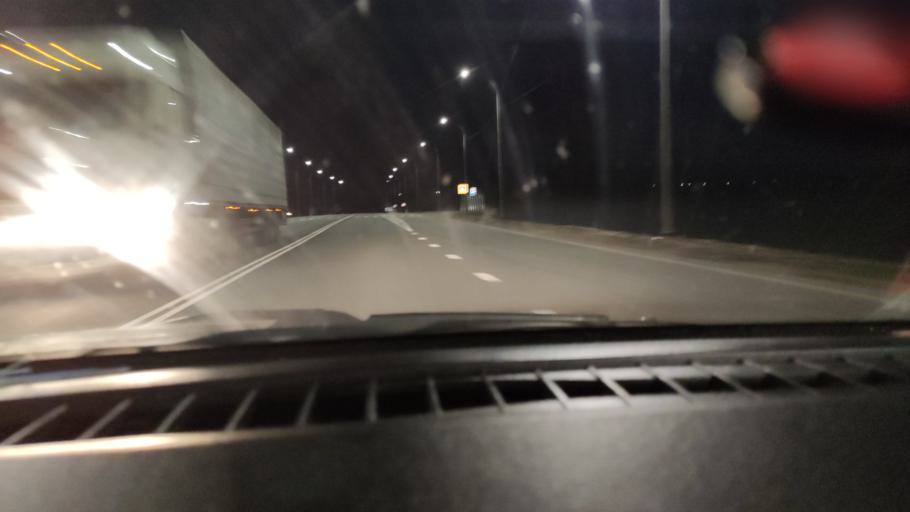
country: RU
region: Saratov
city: Shikhany
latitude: 52.1290
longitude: 47.2336
